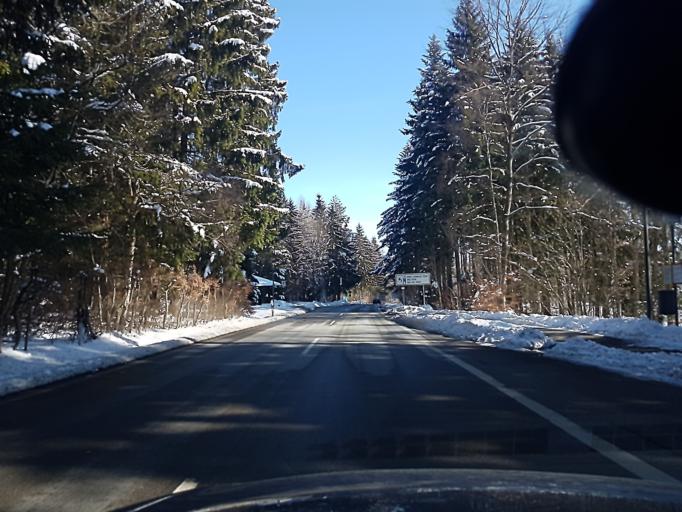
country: DE
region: Baden-Wuerttemberg
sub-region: Freiburg Region
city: Konigsfeld im Schwarzwald
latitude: 48.1358
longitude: 8.4119
